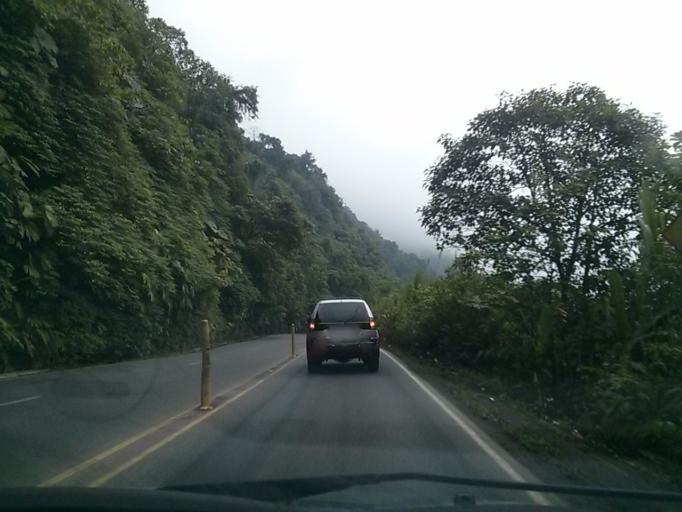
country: CR
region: San Jose
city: Dulce Nombre de Jesus
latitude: 10.0904
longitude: -83.9824
